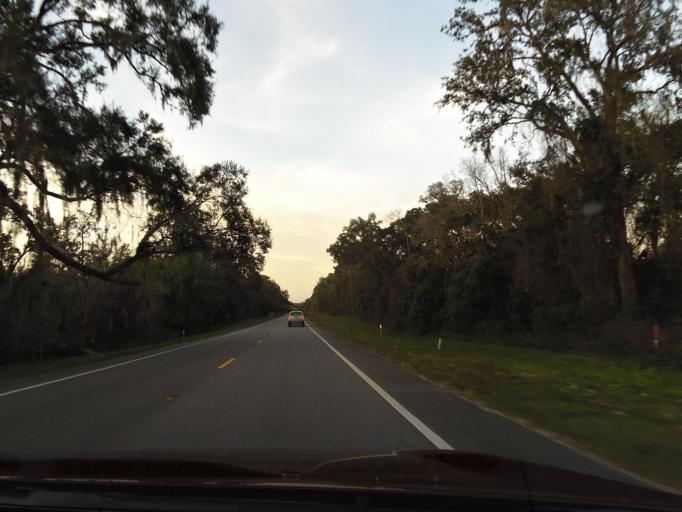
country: US
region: Florida
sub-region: Volusia County
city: De Leon Springs
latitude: 29.1330
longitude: -81.2851
